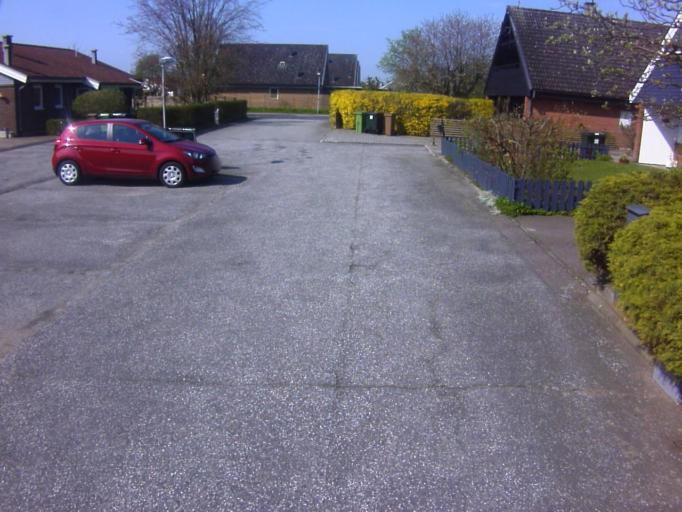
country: SE
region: Skane
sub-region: Kavlinge Kommun
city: Loddekopinge
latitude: 55.7649
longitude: 13.0015
